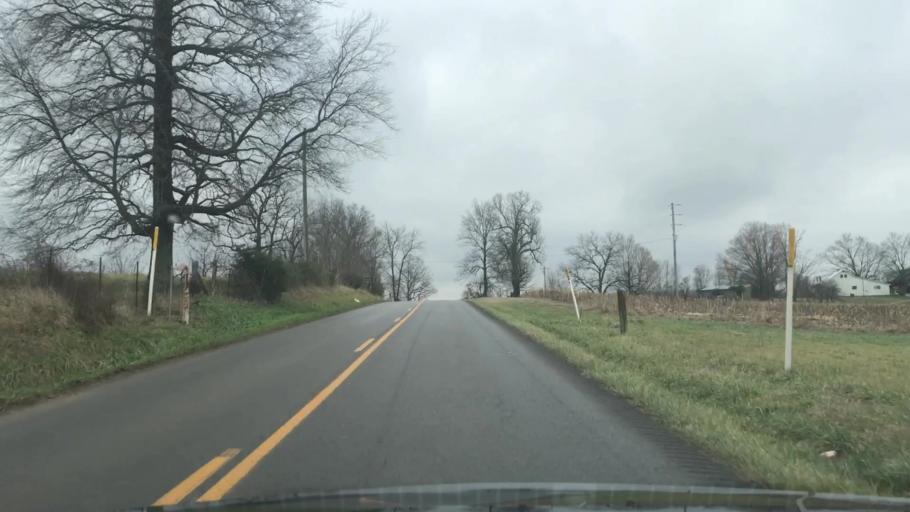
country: US
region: Kentucky
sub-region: Monroe County
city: Tompkinsville
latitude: 36.8282
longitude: -85.7502
